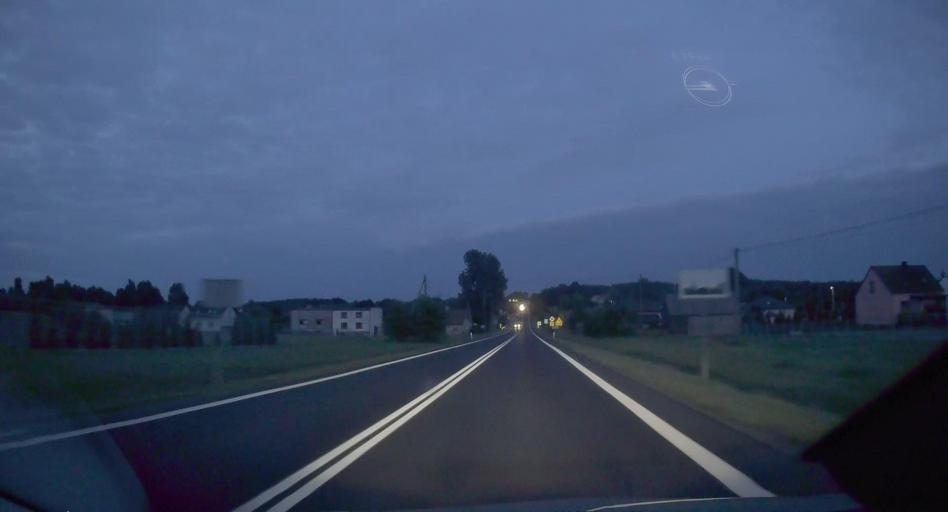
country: PL
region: Silesian Voivodeship
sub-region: Powiat klobucki
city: Lobodno
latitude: 50.8850
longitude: 18.9821
